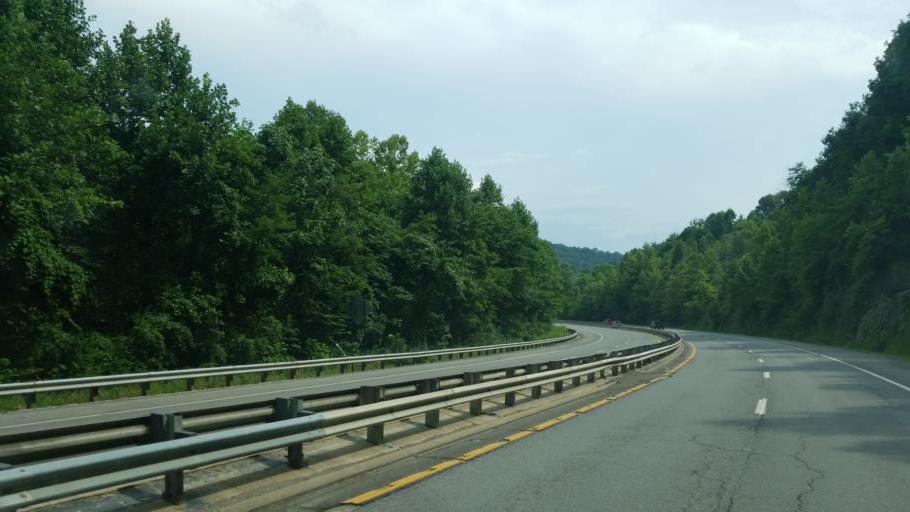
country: US
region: West Virginia
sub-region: Logan County
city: Chapmanville
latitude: 37.9468
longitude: -82.0208
